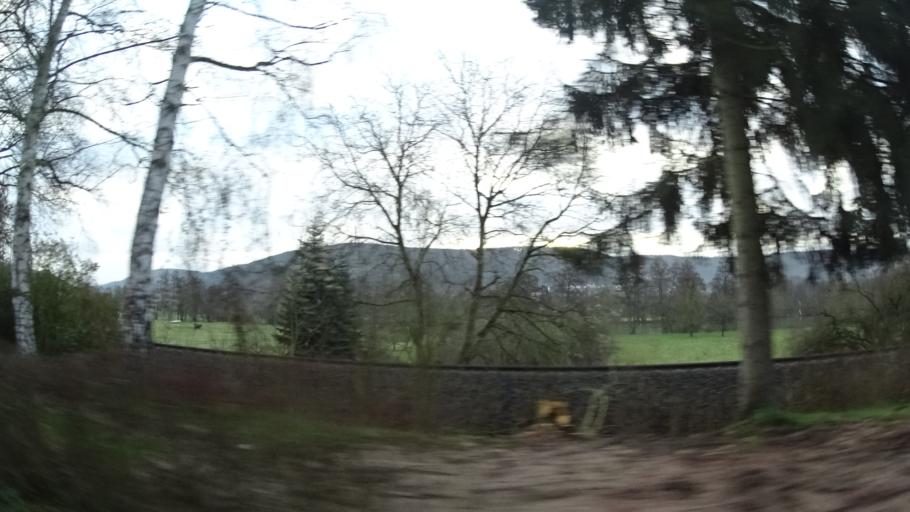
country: DE
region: Baden-Wuerttemberg
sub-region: Regierungsbezirk Stuttgart
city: Freudenberg
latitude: 49.7698
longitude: 9.3146
